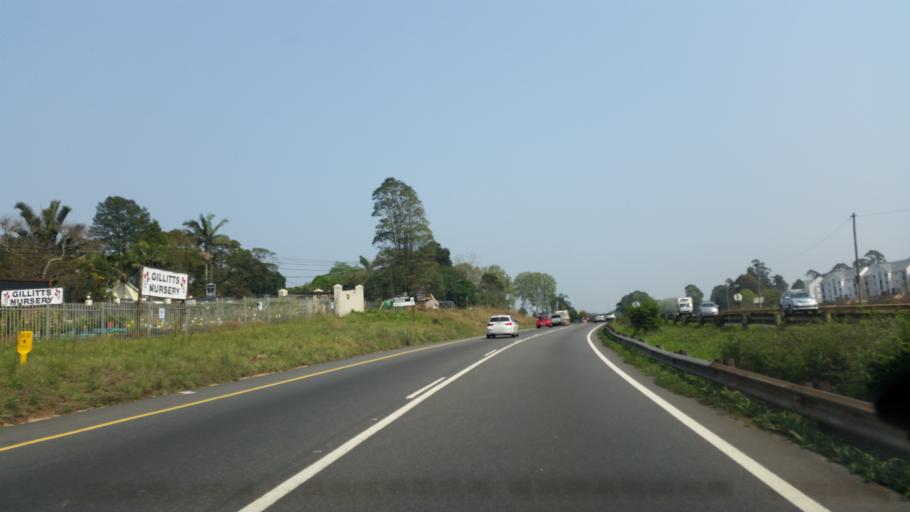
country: ZA
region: KwaZulu-Natal
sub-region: eThekwini Metropolitan Municipality
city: Mpumalanga
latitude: -29.7935
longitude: 30.7879
